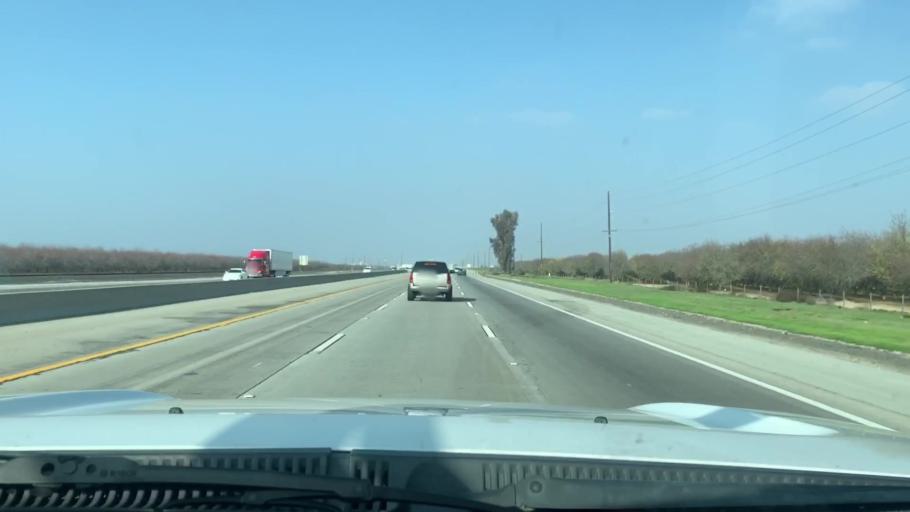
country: US
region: California
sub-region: Kern County
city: Shafter
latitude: 35.5393
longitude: -119.1935
